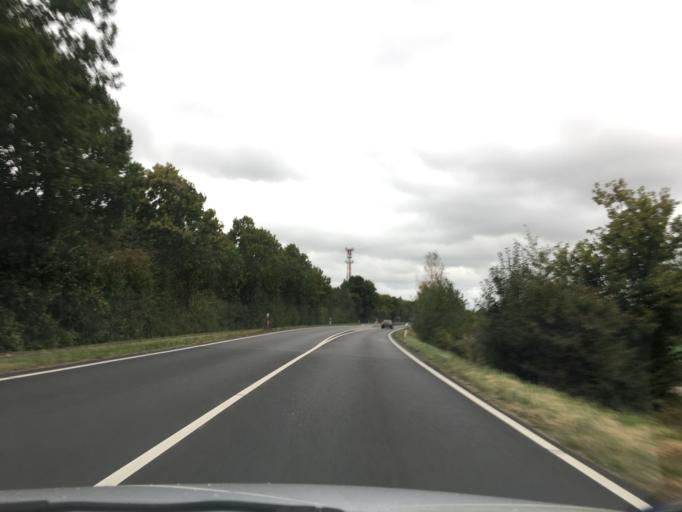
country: DE
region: Schleswig-Holstein
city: Altenholz
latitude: 54.4009
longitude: 10.1352
